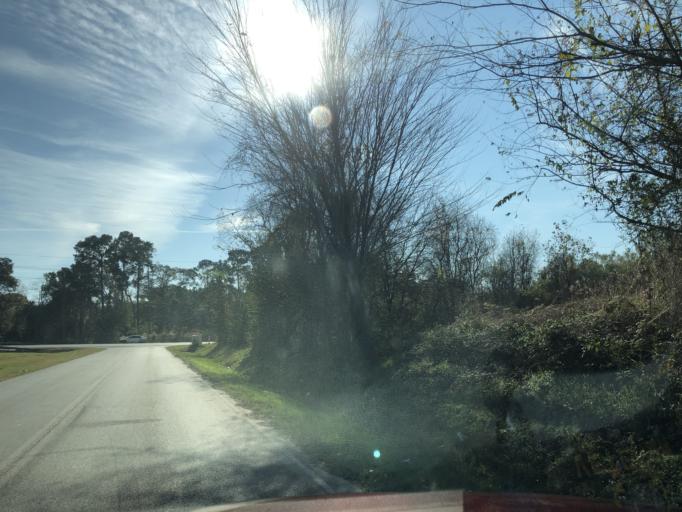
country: US
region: Texas
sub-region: Harris County
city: Tomball
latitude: 30.0427
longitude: -95.5462
